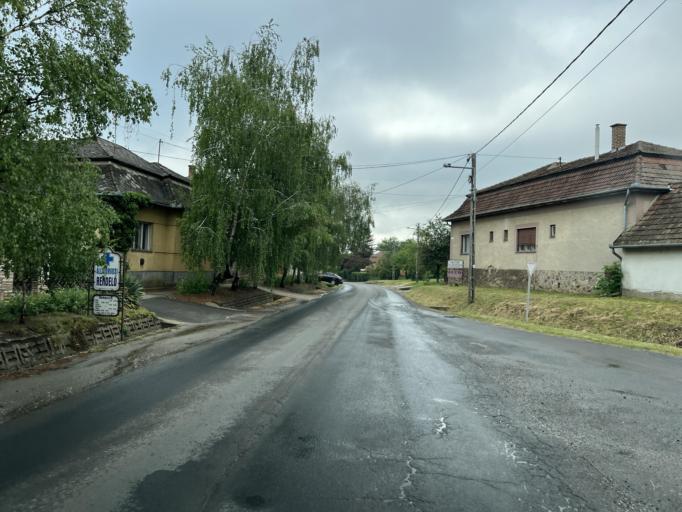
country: HU
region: Pest
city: Galgaheviz
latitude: 47.6223
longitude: 19.5487
